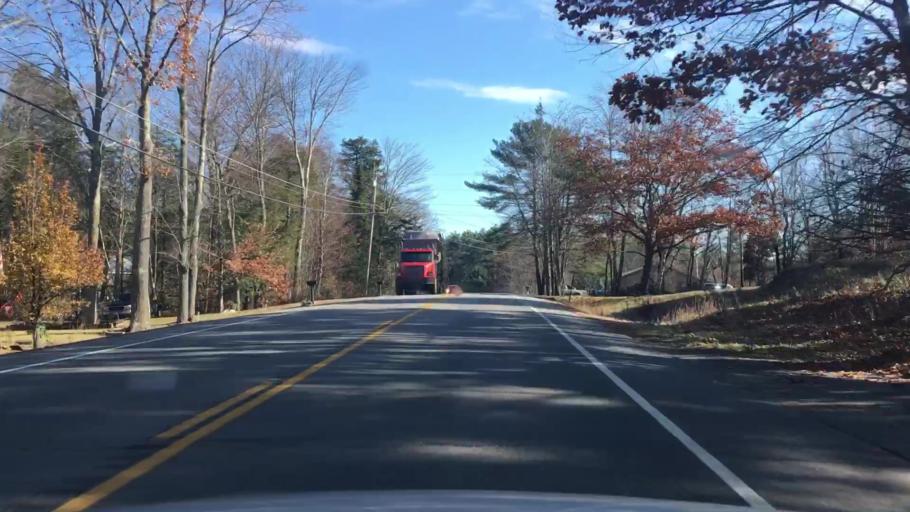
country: US
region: Maine
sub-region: Lincoln County
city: Jefferson
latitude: 44.2494
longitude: -69.5173
